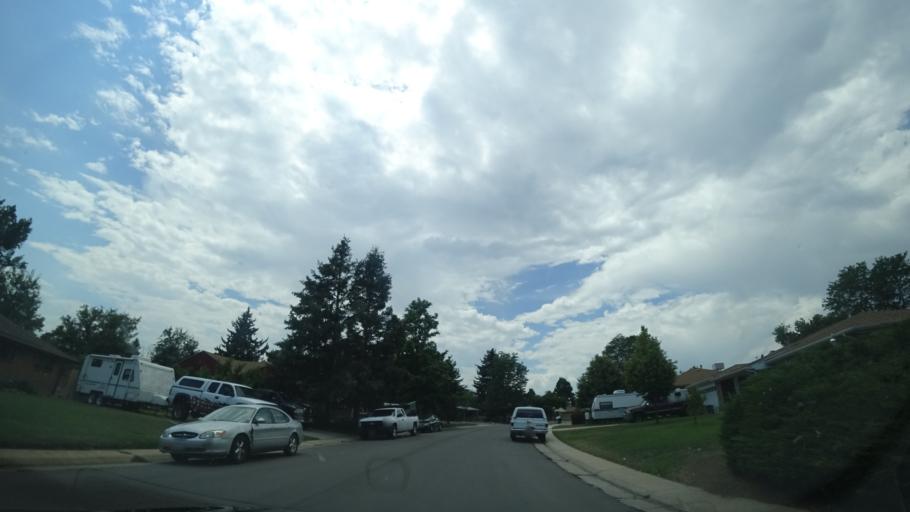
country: US
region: Colorado
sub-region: Jefferson County
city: Lakewood
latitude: 39.7239
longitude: -105.0973
